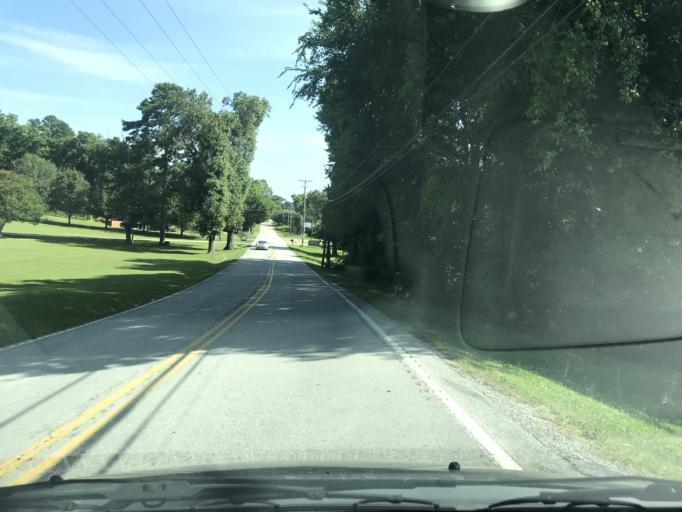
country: US
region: Tennessee
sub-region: Hamilton County
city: Lakesite
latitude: 35.2099
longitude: -85.0653
